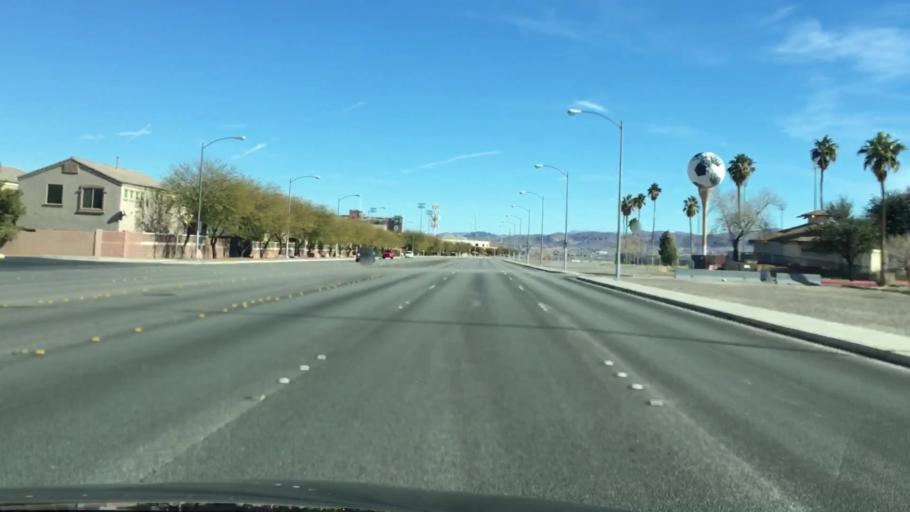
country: US
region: Nevada
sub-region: Clark County
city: Whitney
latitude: 36.0855
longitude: -115.0259
